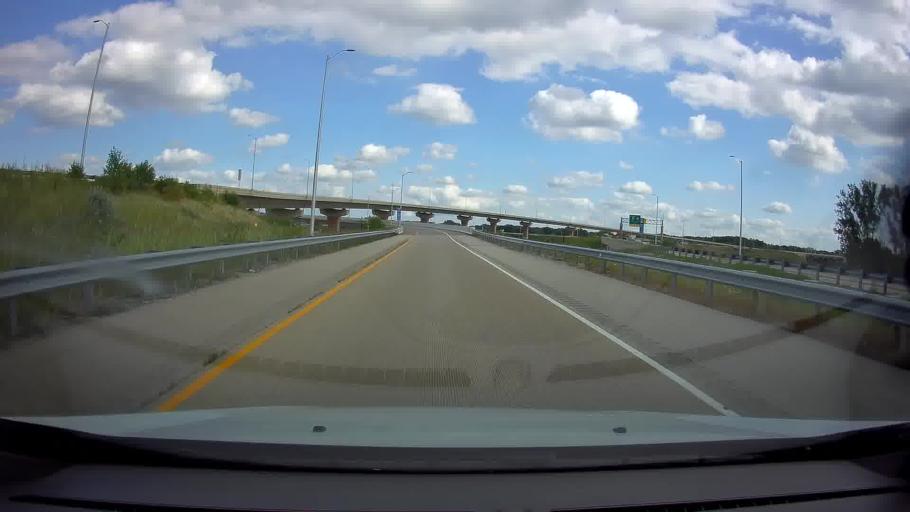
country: US
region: Wisconsin
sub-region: Brown County
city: Howard
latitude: 44.5405
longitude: -88.0826
